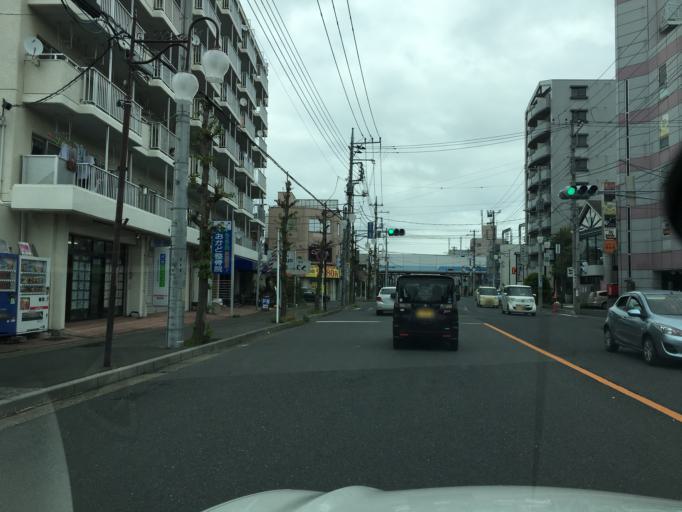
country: JP
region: Saitama
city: Koshigaya
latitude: 35.8649
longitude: 139.7905
